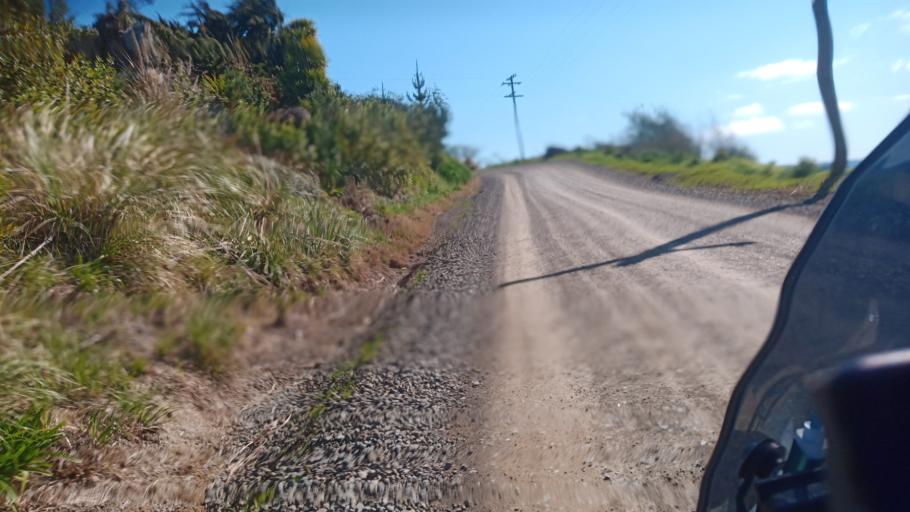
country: NZ
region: Gisborne
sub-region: Gisborne District
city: Gisborne
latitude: -39.1301
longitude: 177.9506
